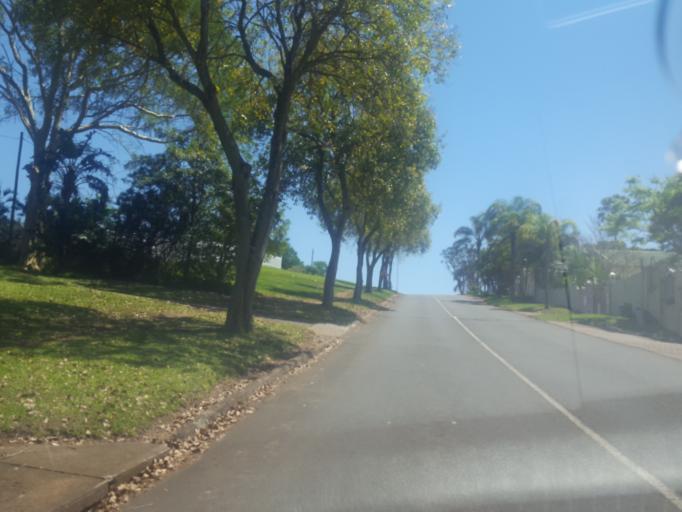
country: ZA
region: KwaZulu-Natal
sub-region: uThungulu District Municipality
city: Empangeni
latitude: -28.7432
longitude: 31.9021
